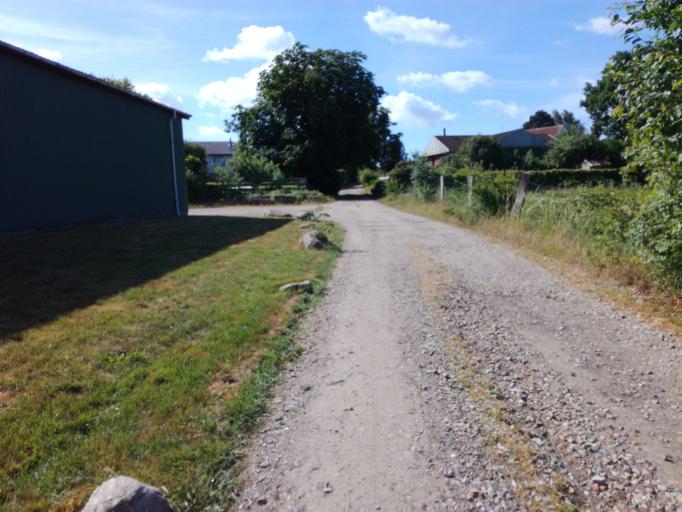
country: DK
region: South Denmark
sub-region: Fredericia Kommune
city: Fredericia
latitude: 55.6188
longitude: 9.7749
